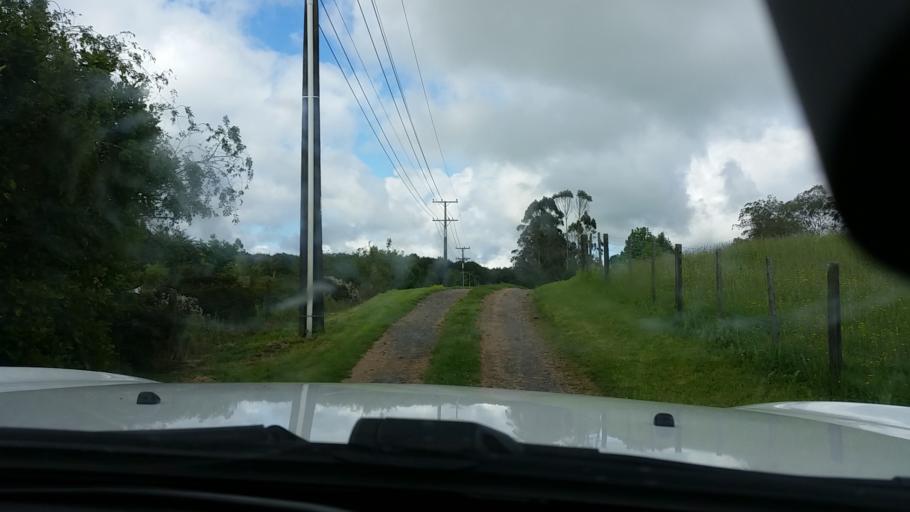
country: NZ
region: Bay of Plenty
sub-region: Rotorua District
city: Rotorua
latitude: -38.0903
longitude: 176.0770
